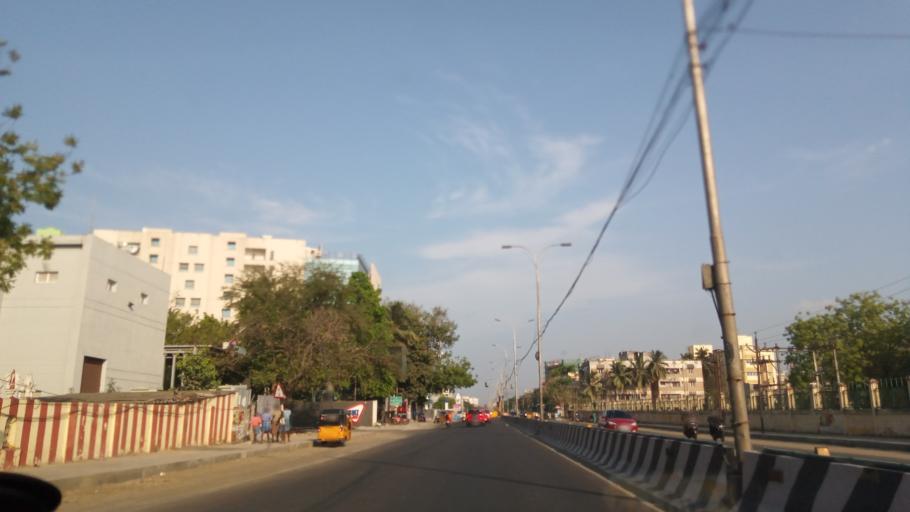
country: IN
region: Tamil Nadu
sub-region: Thiruvallur
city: Porur
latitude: 13.0301
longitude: 80.1675
